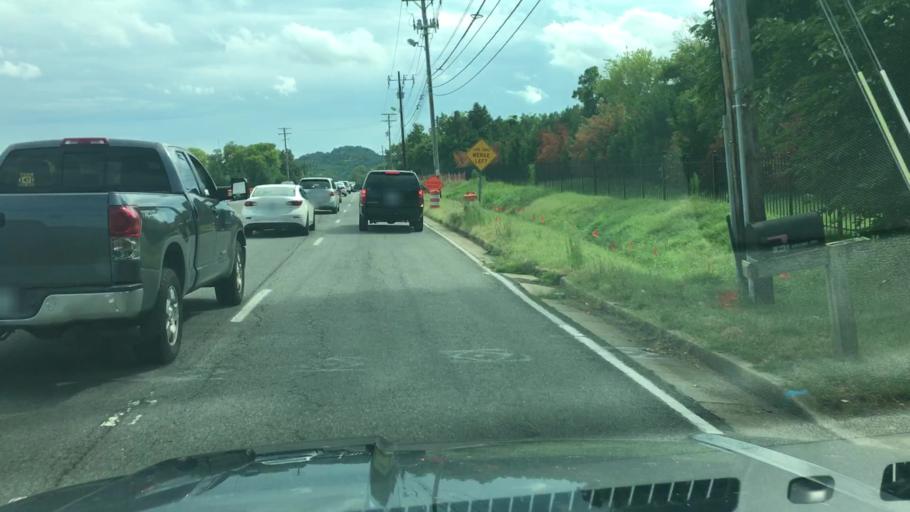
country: US
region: Tennessee
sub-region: Williamson County
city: Brentwood Estates
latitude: 35.9990
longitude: -86.8095
